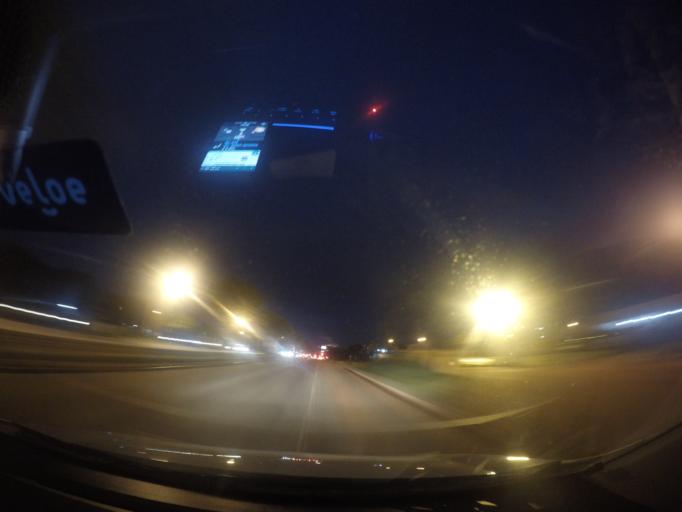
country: BR
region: Goias
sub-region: Goiania
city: Goiania
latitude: -16.6242
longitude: -49.2507
